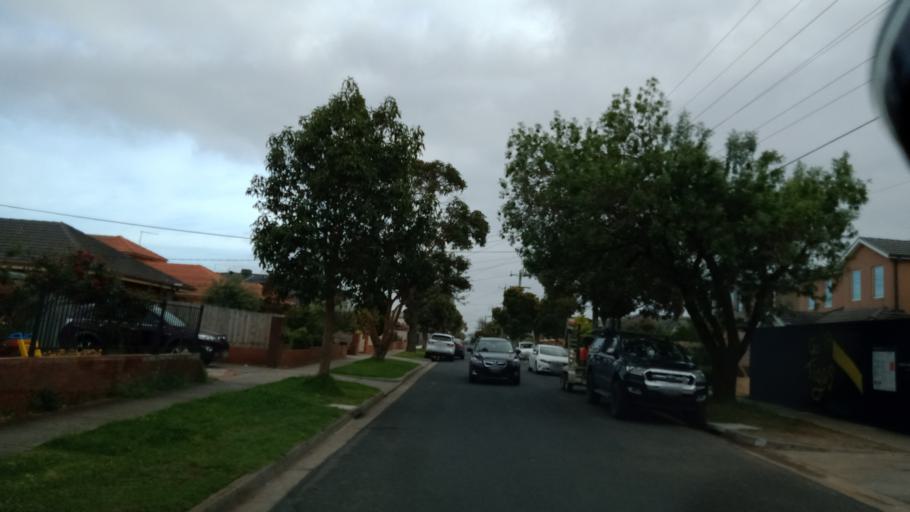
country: AU
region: Victoria
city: McKinnon
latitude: -37.9316
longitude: 145.0661
